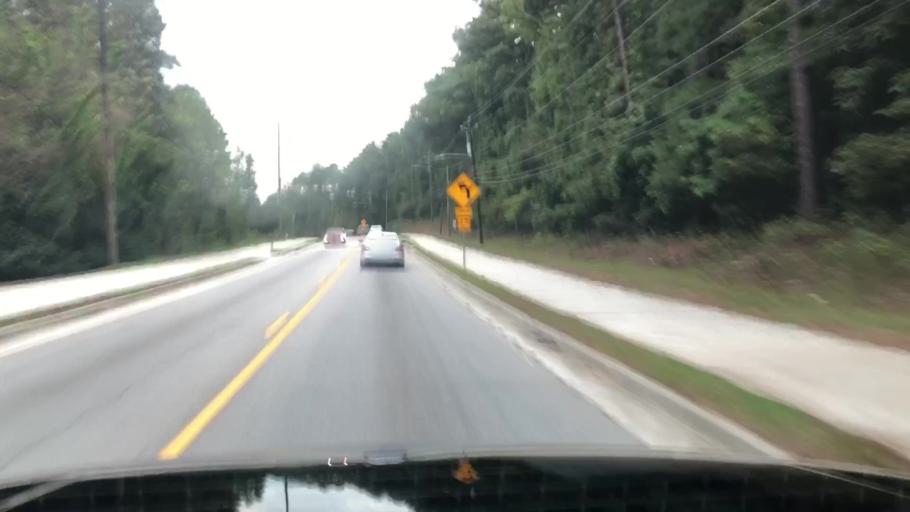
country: US
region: Georgia
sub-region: Cobb County
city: Mableton
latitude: 33.7076
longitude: -84.5555
